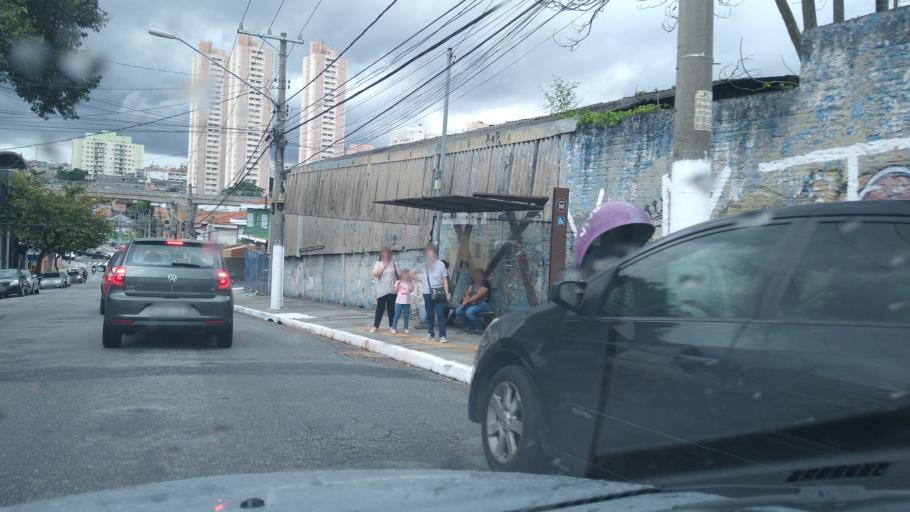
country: BR
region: Sao Paulo
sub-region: Sao Caetano Do Sul
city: Sao Caetano do Sul
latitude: -23.5908
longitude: -46.5451
